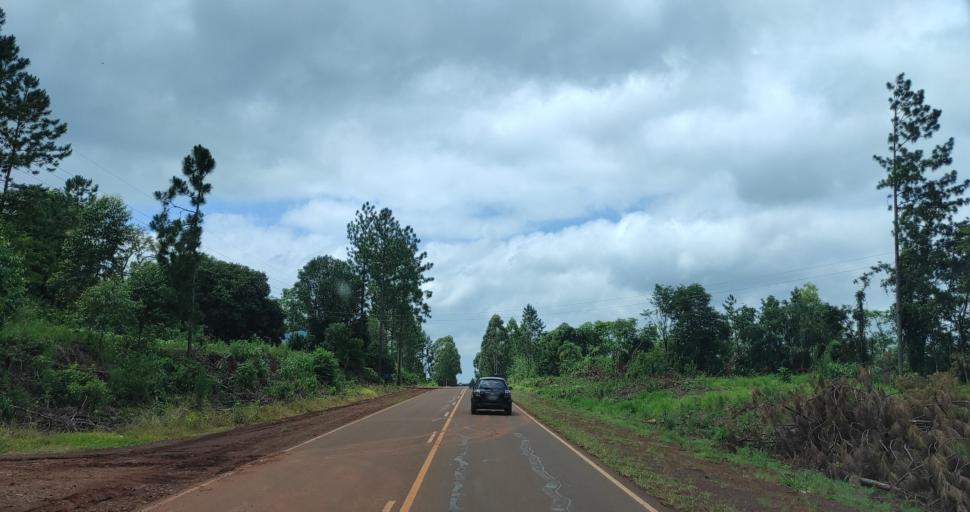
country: AR
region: Misiones
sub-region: Departamento de Veinticinco de Mayo
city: Veinticinco de Mayo
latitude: -27.4147
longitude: -54.7378
